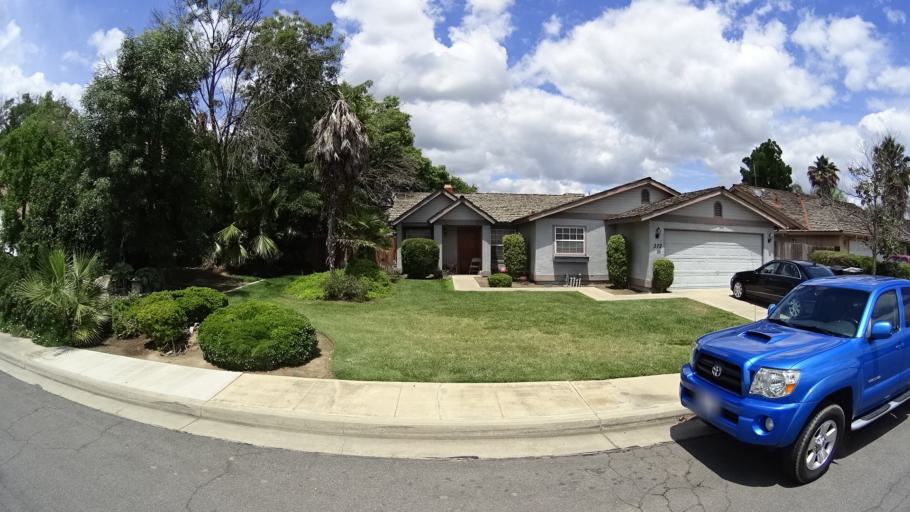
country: US
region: California
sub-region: Kings County
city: Lucerne
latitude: 36.3581
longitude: -119.6485
